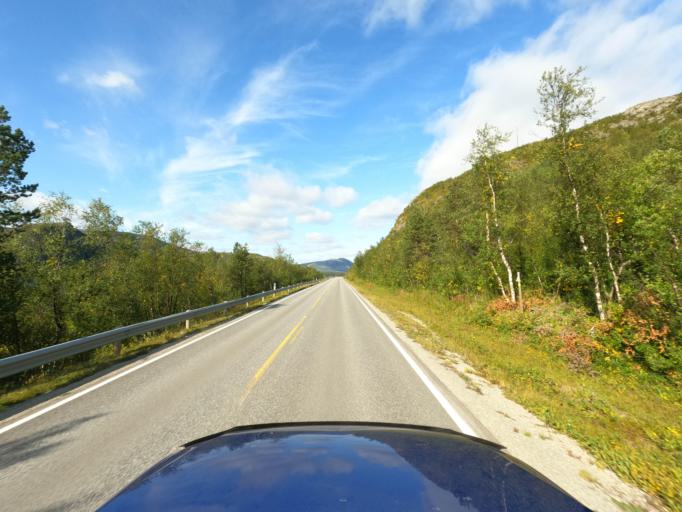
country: NO
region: Finnmark Fylke
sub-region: Porsanger
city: Lakselv
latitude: 69.9138
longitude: 24.9851
